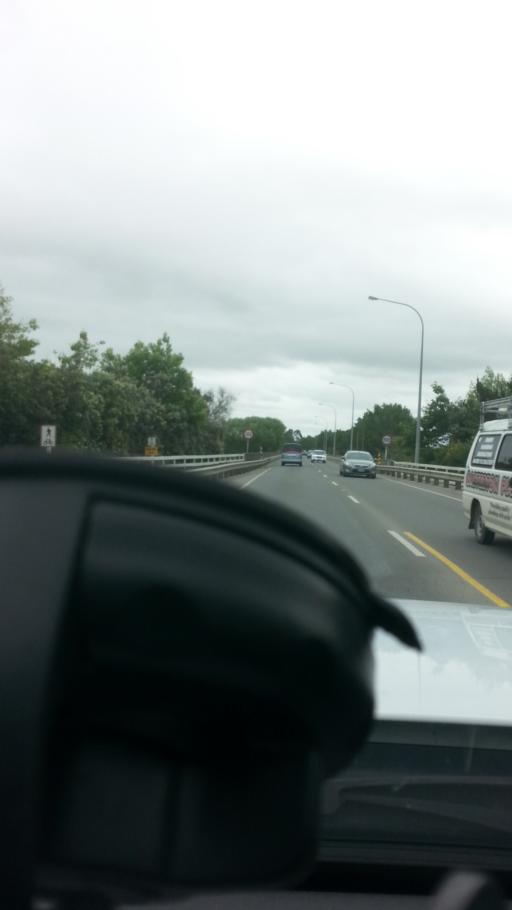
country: NZ
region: Wellington
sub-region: Masterton District
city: Masterton
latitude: -40.9635
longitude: 175.6110
